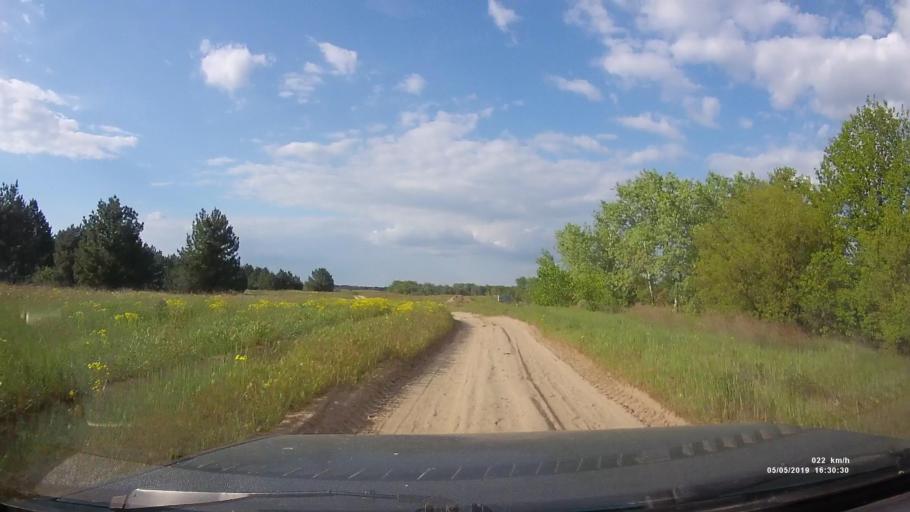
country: RU
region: Rostov
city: Ust'-Donetskiy
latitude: 47.7737
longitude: 41.0158
